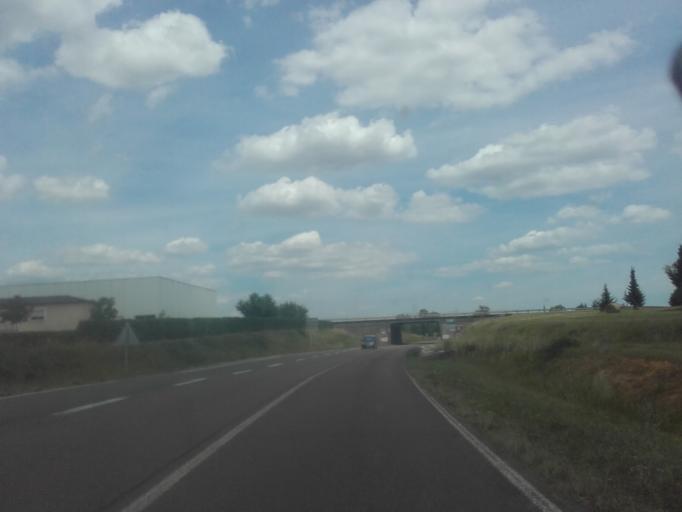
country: FR
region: Bourgogne
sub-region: Departement de la Cote-d'Or
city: Corpeau
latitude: 46.9269
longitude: 4.7411
